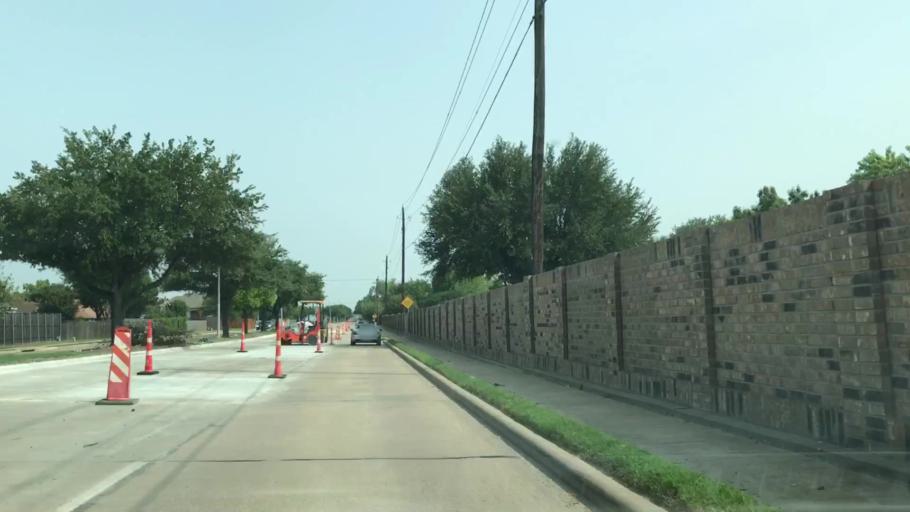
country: US
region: Texas
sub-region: Dallas County
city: Rowlett
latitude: 32.9193
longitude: -96.5757
